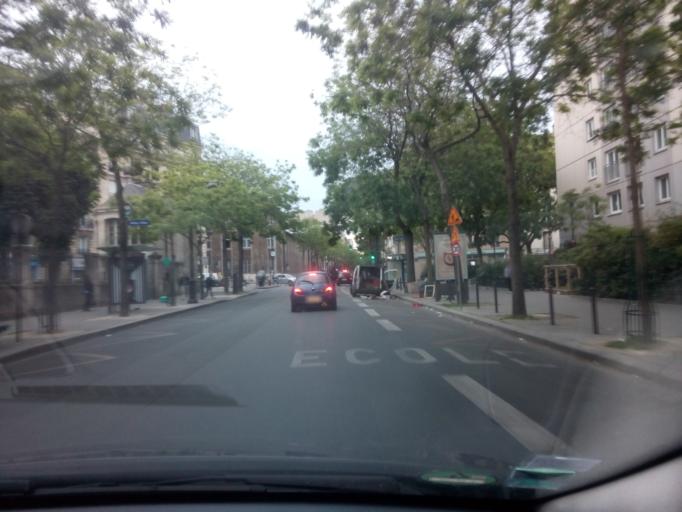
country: FR
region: Ile-de-France
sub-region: Departement des Hauts-de-Seine
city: Montrouge
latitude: 48.8309
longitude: 2.3181
